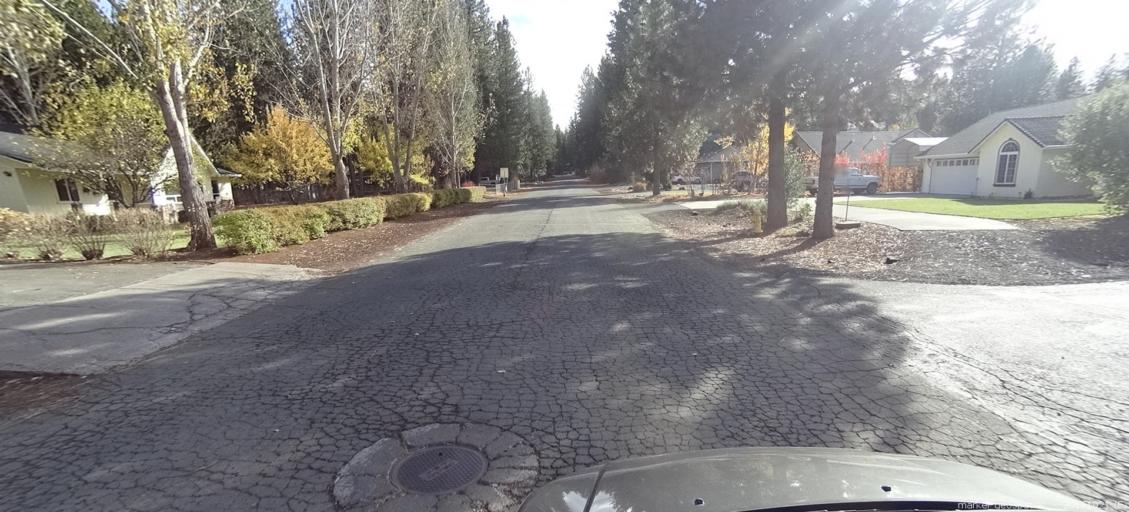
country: US
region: California
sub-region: Shasta County
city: Burney
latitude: 40.8730
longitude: -121.6694
